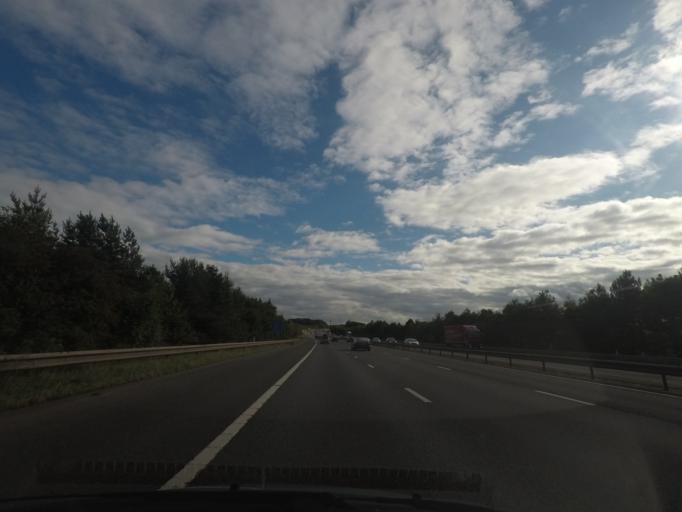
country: GB
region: England
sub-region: Leicestershire
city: Shepshed
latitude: 52.7320
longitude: -1.2822
